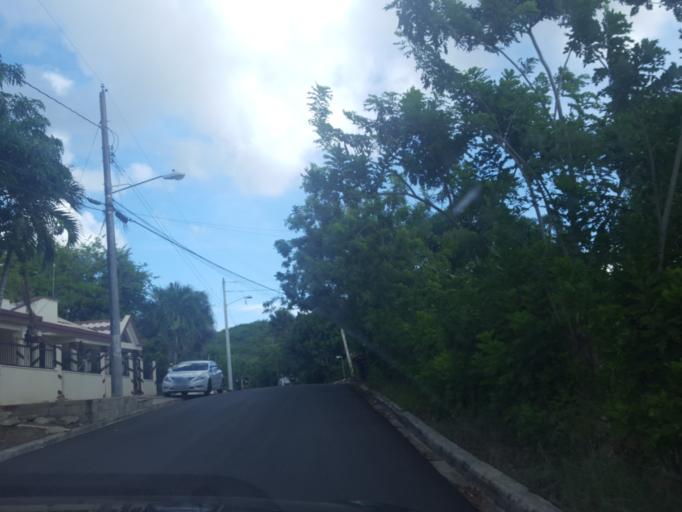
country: DO
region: Santiago
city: Licey al Medio
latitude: 19.3670
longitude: -70.6314
